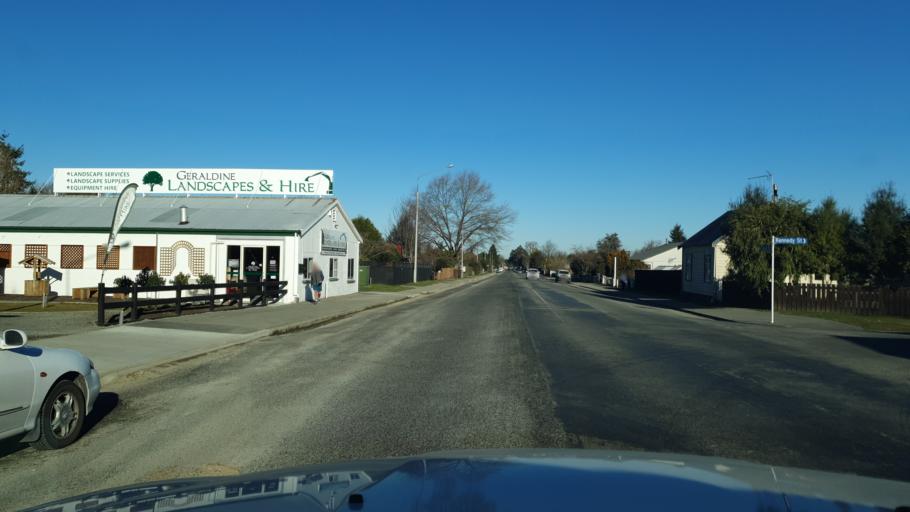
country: NZ
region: Canterbury
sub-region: Timaru District
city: Pleasant Point
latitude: -44.1041
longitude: 171.2448
